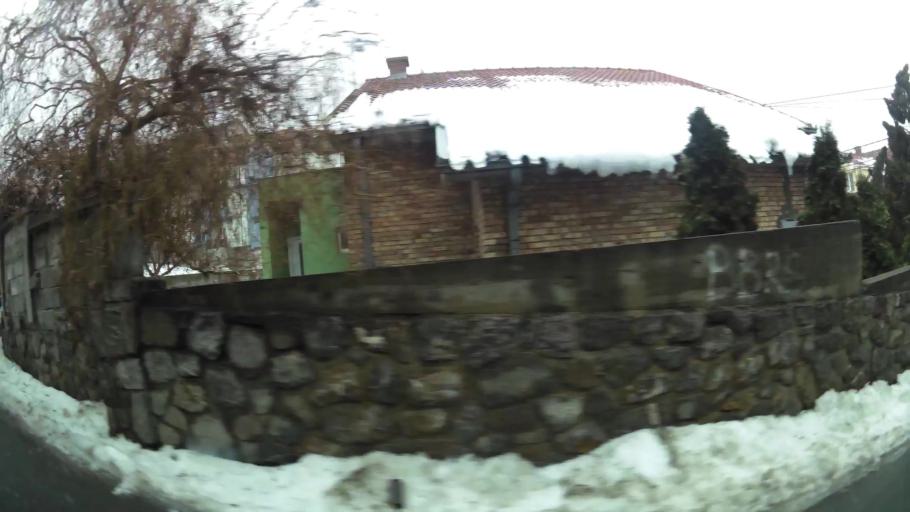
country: RS
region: Central Serbia
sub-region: Belgrade
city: Zvezdara
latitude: 44.7851
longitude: 20.5286
